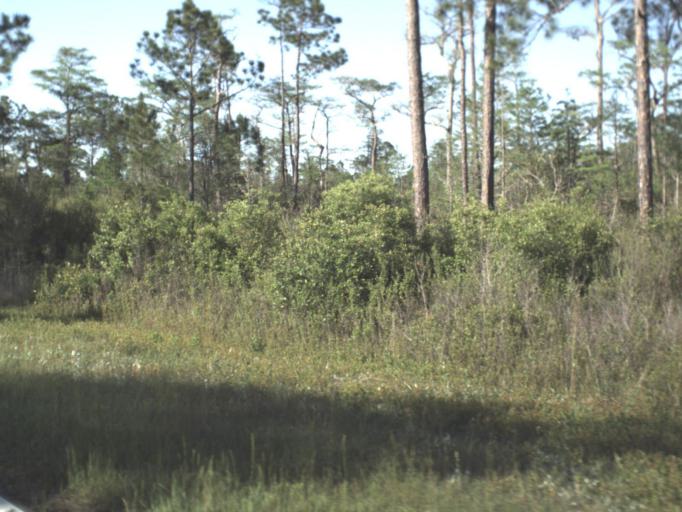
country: US
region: Florida
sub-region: Gulf County
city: Wewahitchka
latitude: 30.0909
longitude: -84.9842
